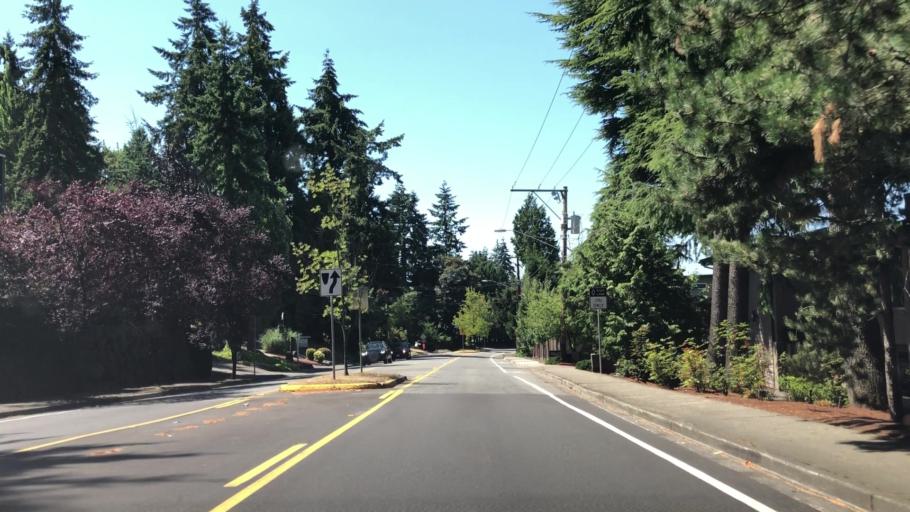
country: US
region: Washington
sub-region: King County
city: Kirkland
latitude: 47.6679
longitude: -122.1893
